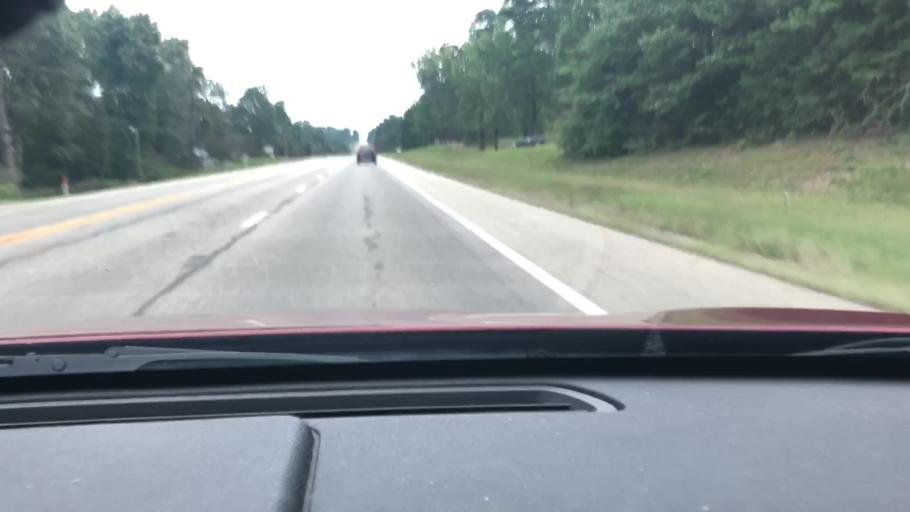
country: US
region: Arkansas
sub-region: Miller County
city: Texarkana
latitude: 33.4296
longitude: -93.9545
